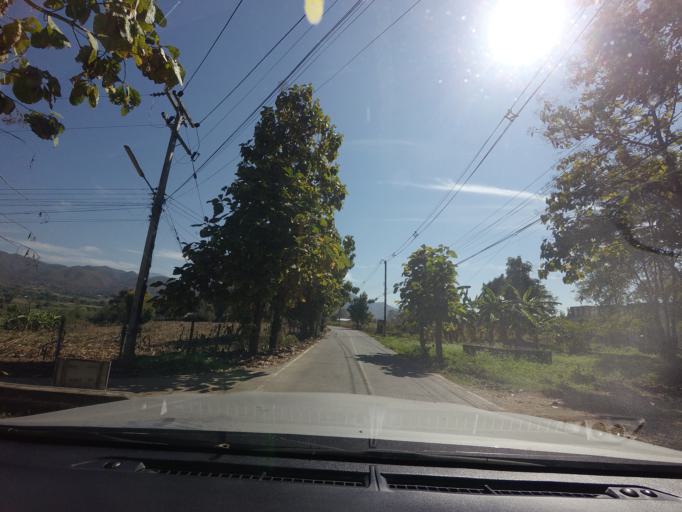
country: TH
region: Mae Hong Son
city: Wiang Nuea
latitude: 19.3868
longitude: 98.4348
